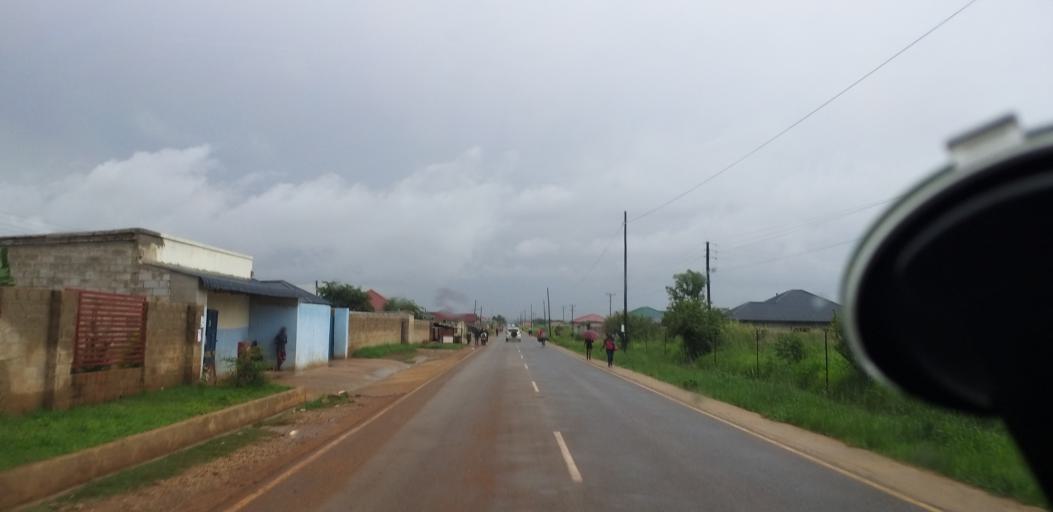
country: ZM
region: Lusaka
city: Lusaka
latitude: -15.5084
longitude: 28.3117
